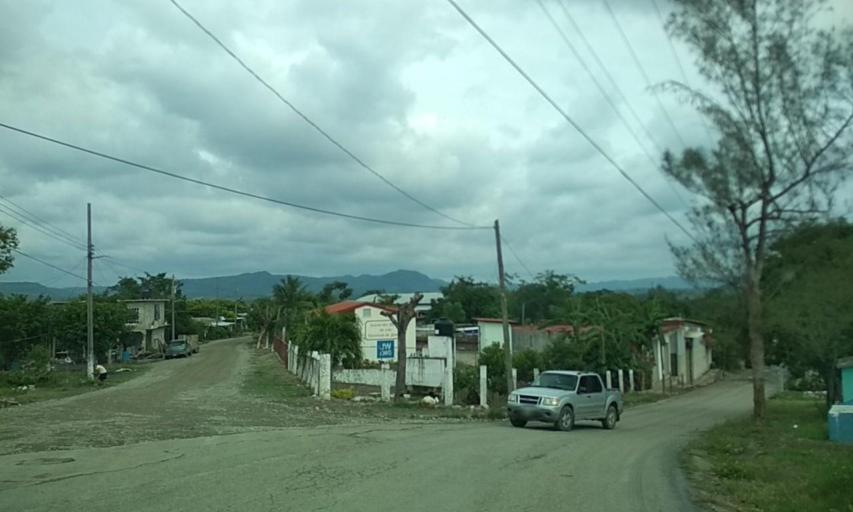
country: MX
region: Veracruz
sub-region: Papantla
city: El Chote
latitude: 20.3579
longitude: -97.3409
